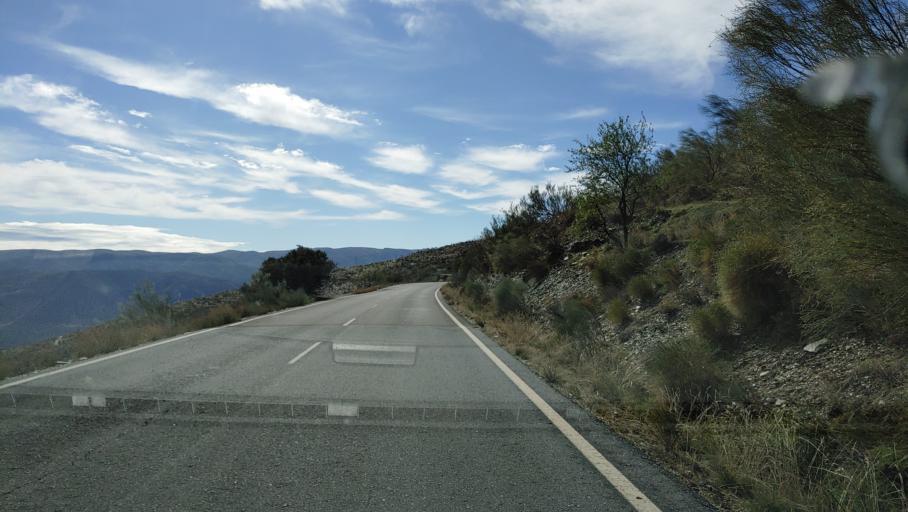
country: ES
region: Andalusia
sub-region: Provincia de Almeria
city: Ohanes
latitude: 37.0486
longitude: -2.7317
